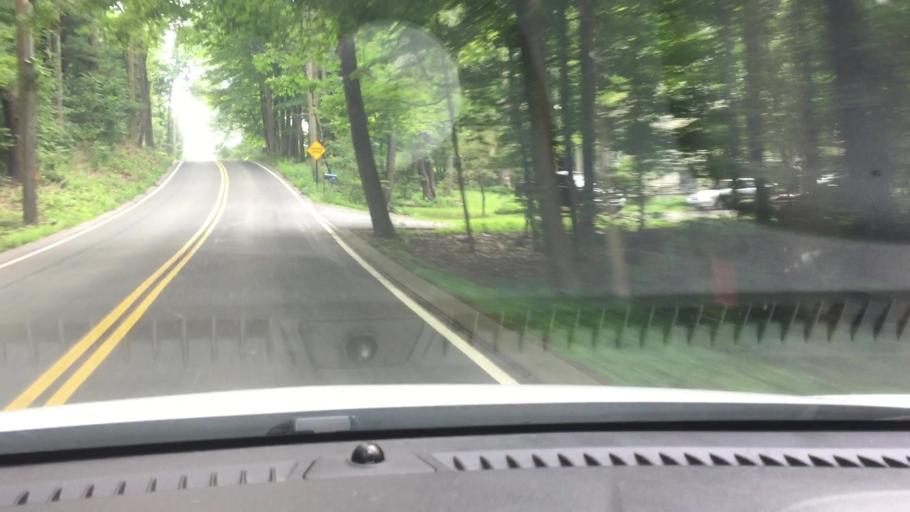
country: US
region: Massachusetts
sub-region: Berkshire County
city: Pittsfield
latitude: 42.4882
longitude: -73.2638
